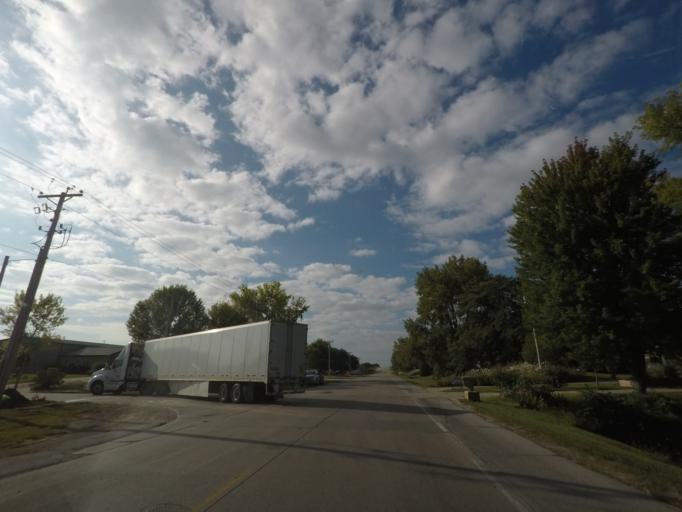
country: US
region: Iowa
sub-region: Story County
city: Nevada
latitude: 42.0100
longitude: -93.4446
